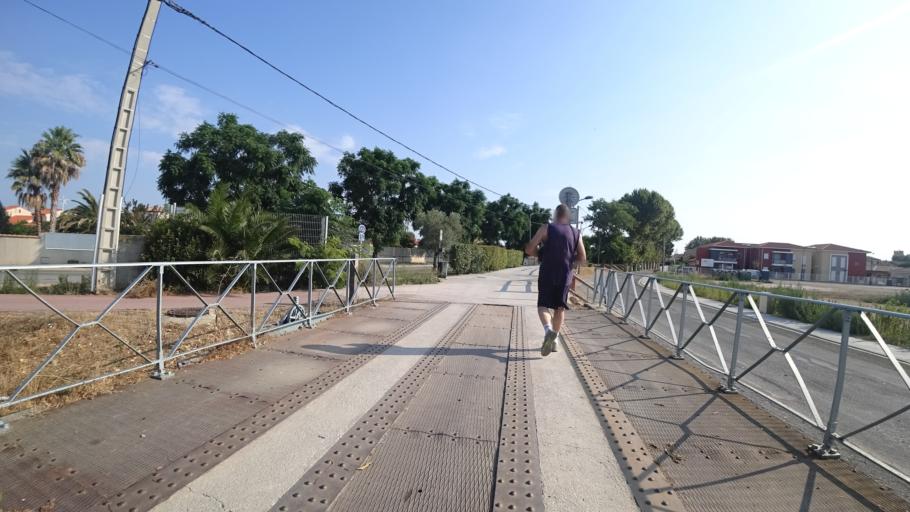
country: FR
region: Languedoc-Roussillon
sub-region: Departement des Pyrenees-Orientales
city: Claira
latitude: 42.7583
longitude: 2.9514
